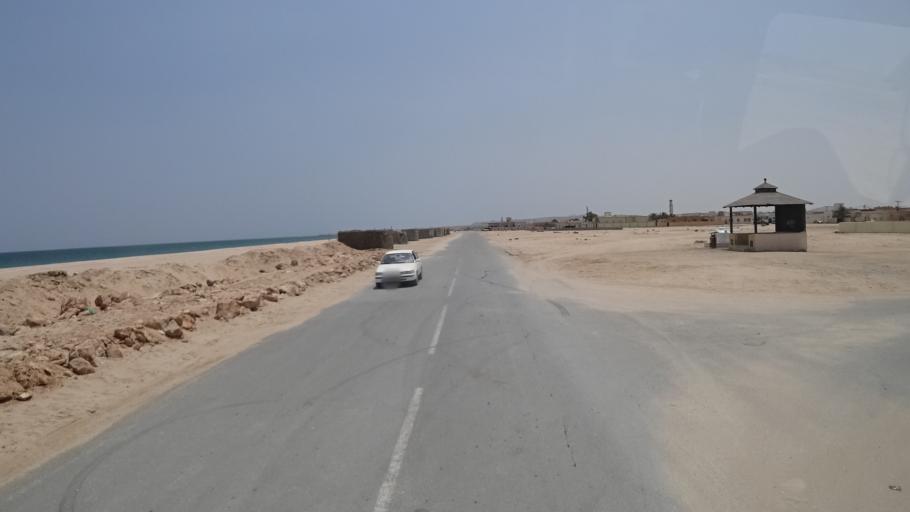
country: OM
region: Ash Sharqiyah
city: Sur
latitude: 22.5237
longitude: 59.7982
